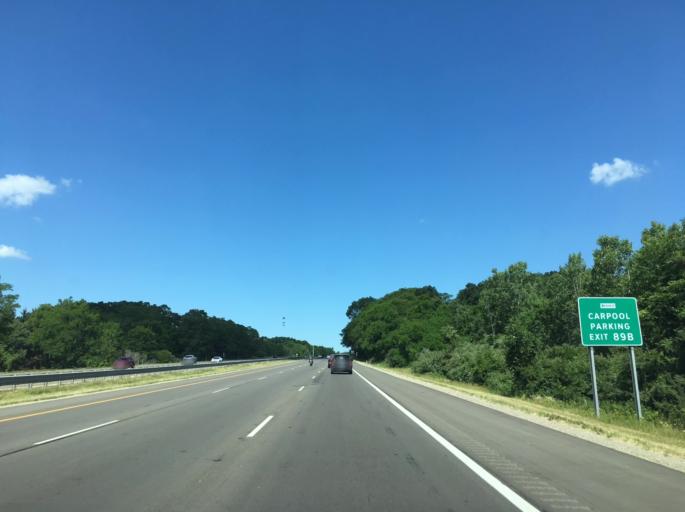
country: US
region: Michigan
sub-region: Oakland County
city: Clarkston
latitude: 42.7294
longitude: -83.3655
